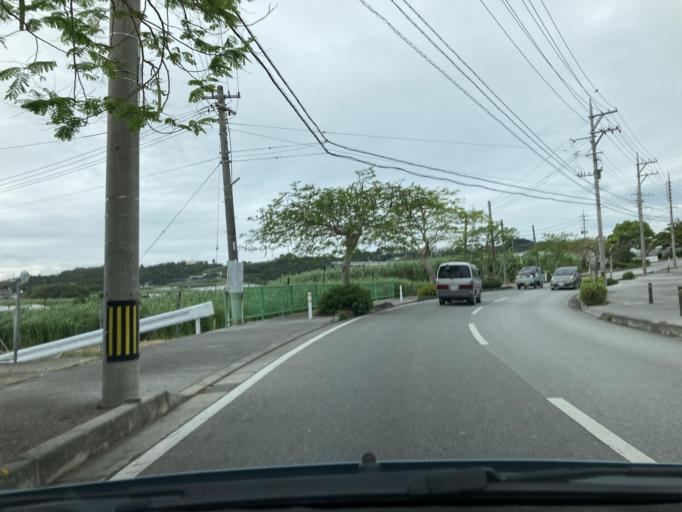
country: JP
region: Okinawa
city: Tomigusuku
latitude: 26.1724
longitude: 127.7135
